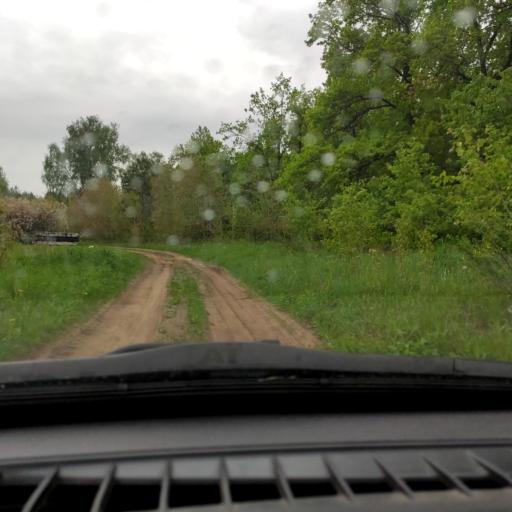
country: RU
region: Samara
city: Zhigulevsk
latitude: 53.5183
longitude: 49.5531
